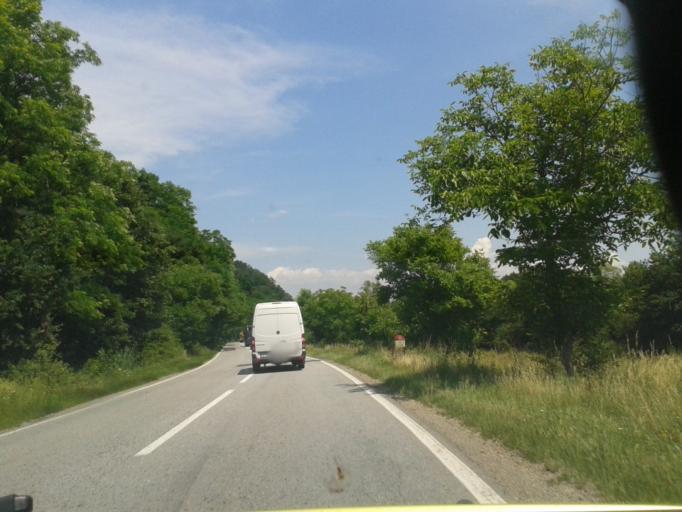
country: RO
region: Hunedoara
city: Lapugiu de Jos
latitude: 45.8976
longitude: 22.4897
